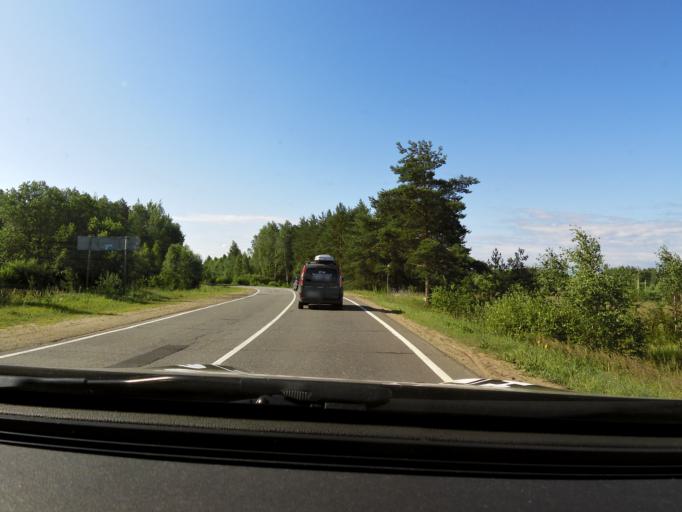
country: RU
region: Tverskaya
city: Zavidovo
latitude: 56.5993
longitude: 36.5377
